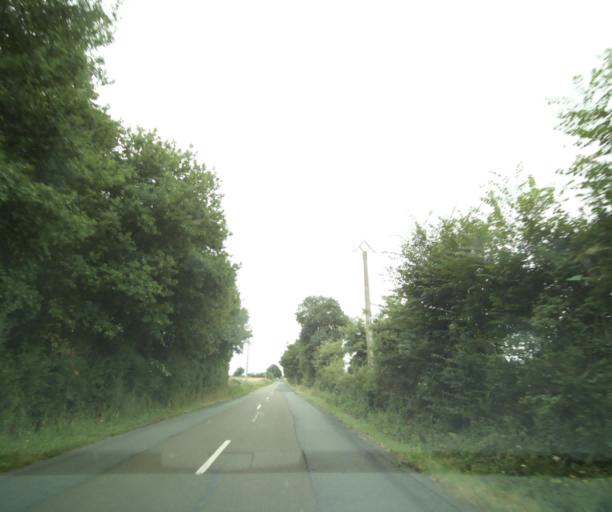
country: FR
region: Pays de la Loire
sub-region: Departement de Maine-et-Loire
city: Durtal
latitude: 47.7324
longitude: -0.2650
